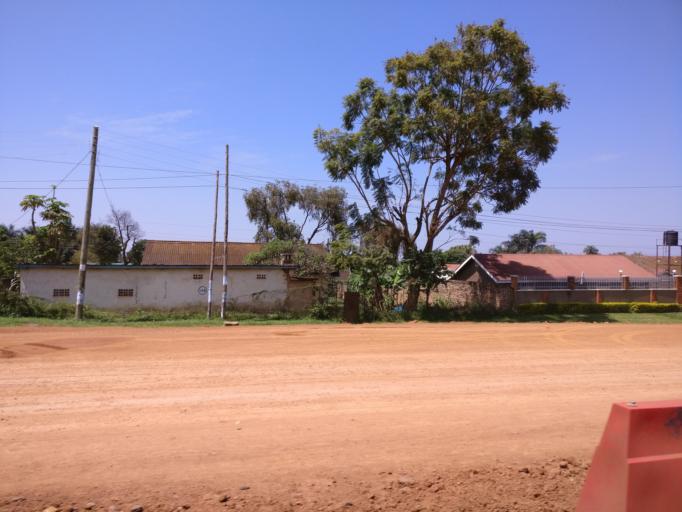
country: UG
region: Central Region
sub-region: Wakiso District
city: Entebbe
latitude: 0.0756
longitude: 32.4788
